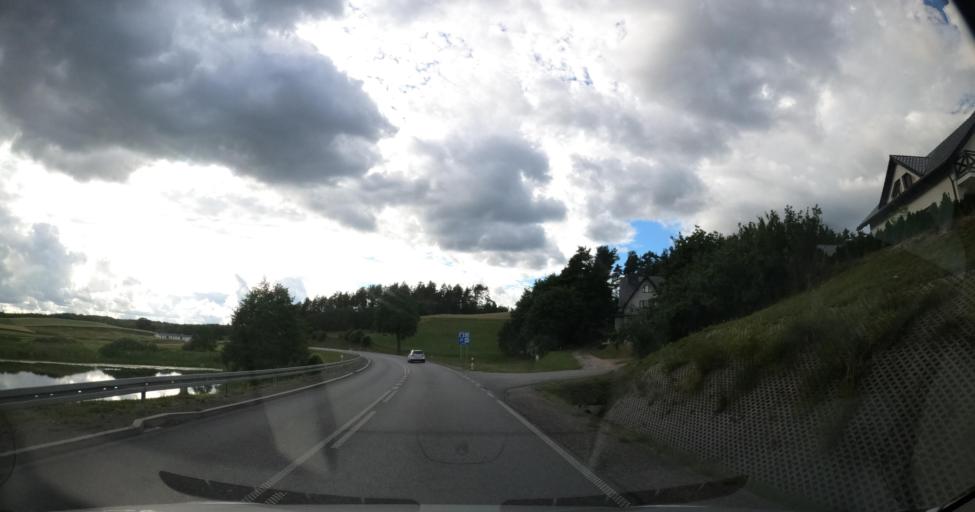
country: PL
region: Pomeranian Voivodeship
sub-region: Powiat kartuski
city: Chmielno
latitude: 54.3420
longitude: 18.0143
